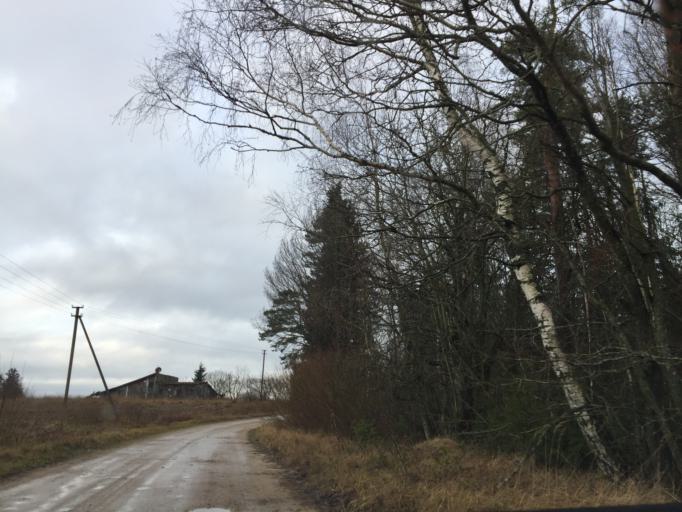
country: LV
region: Vainode
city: Vainode
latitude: 56.6049
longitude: 21.8000
